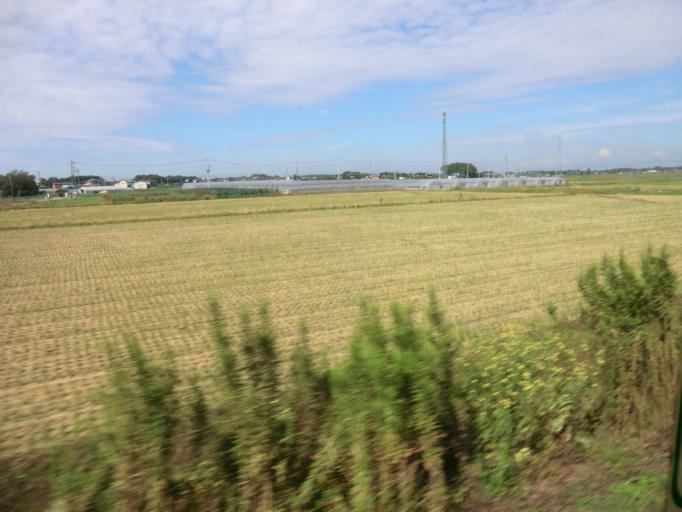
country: JP
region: Ibaraki
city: Ishige
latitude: 36.0826
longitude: 139.9801
